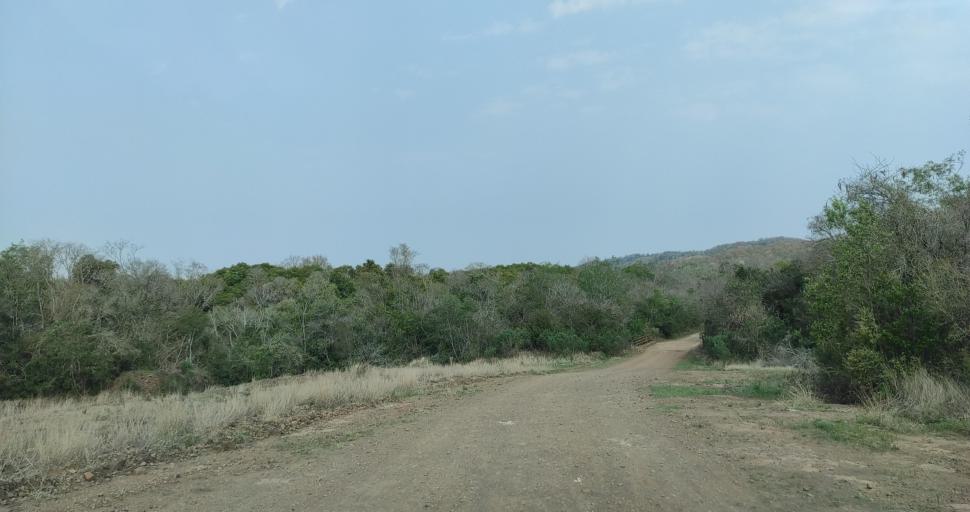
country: AR
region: Misiones
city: Cerro Cora
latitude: -27.5913
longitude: -55.5785
